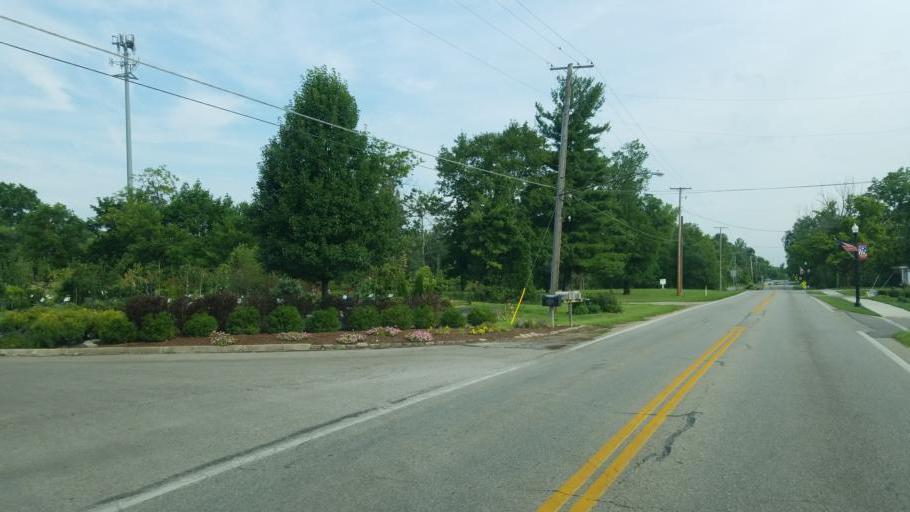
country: US
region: Ohio
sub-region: Delaware County
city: Powell
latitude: 40.1625
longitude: -83.1355
